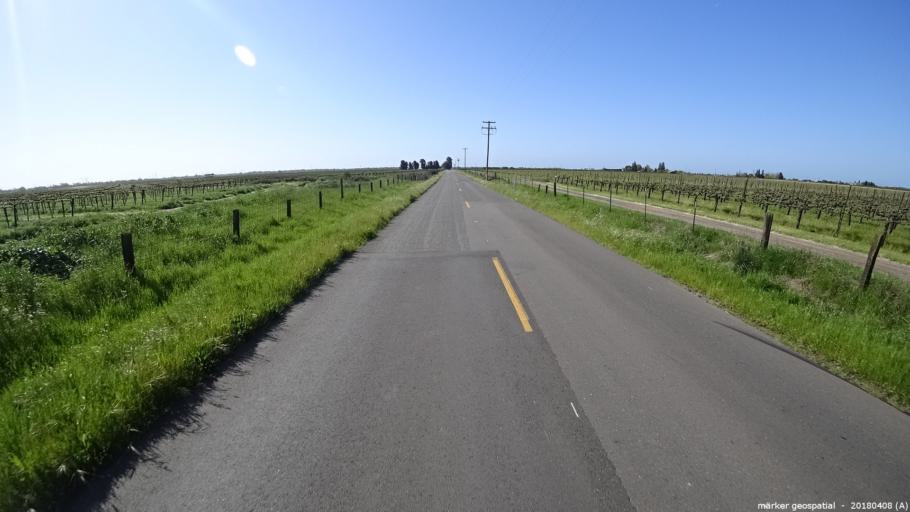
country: US
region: California
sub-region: Sacramento County
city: Elk Grove
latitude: 38.3580
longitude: -121.3712
